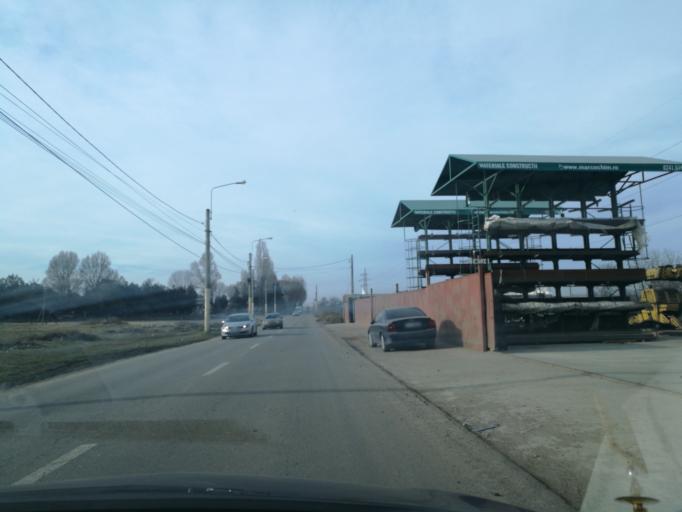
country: RO
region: Constanta
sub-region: Municipiul Constanta
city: Constanta
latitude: 44.1894
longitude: 28.6099
